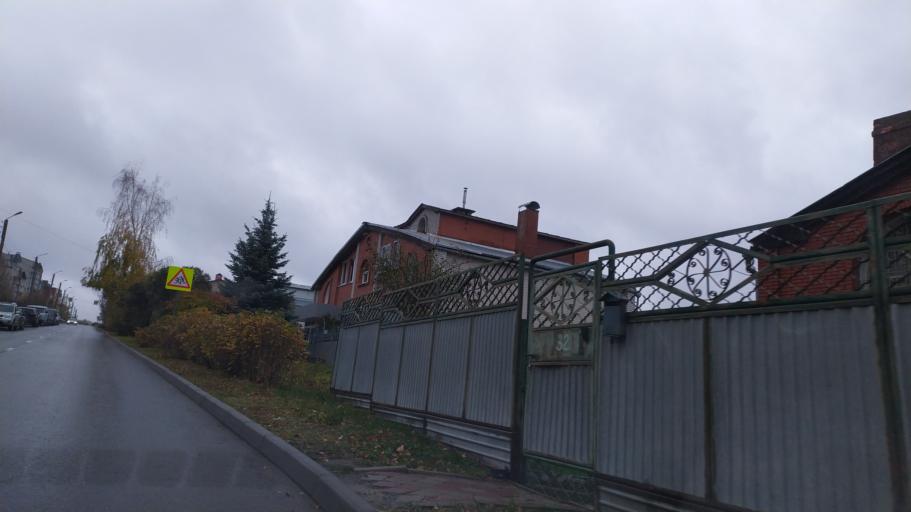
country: RU
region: Chuvashia
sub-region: Cheboksarskiy Rayon
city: Cheboksary
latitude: 56.1476
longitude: 47.1621
